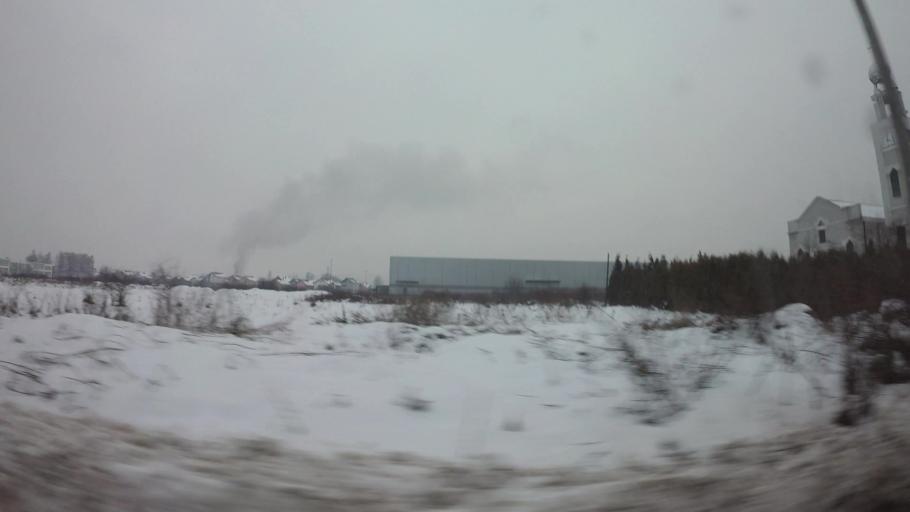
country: BA
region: Federation of Bosnia and Herzegovina
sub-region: Kanton Sarajevo
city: Sarajevo
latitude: 43.8452
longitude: 18.3070
